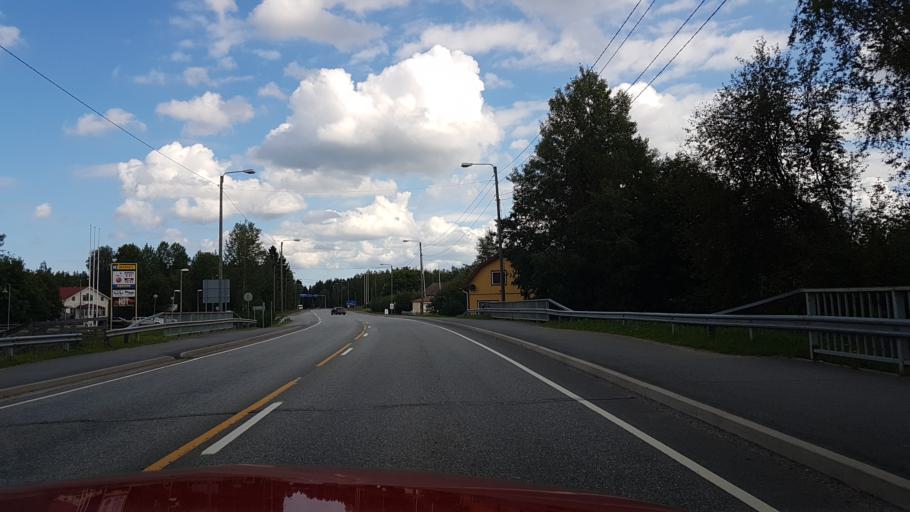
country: FI
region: Northern Ostrobothnia
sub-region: Ylivieska
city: Himanka
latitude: 64.0625
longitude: 23.6558
